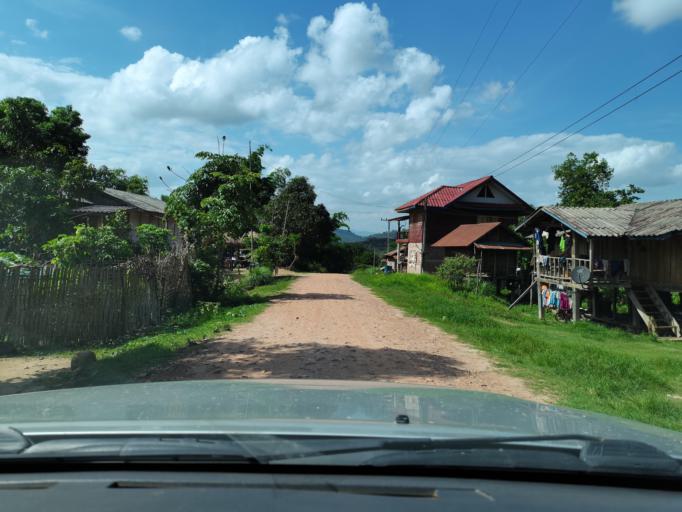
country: LA
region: Loungnamtha
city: Muang Nale
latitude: 20.5794
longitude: 101.0591
